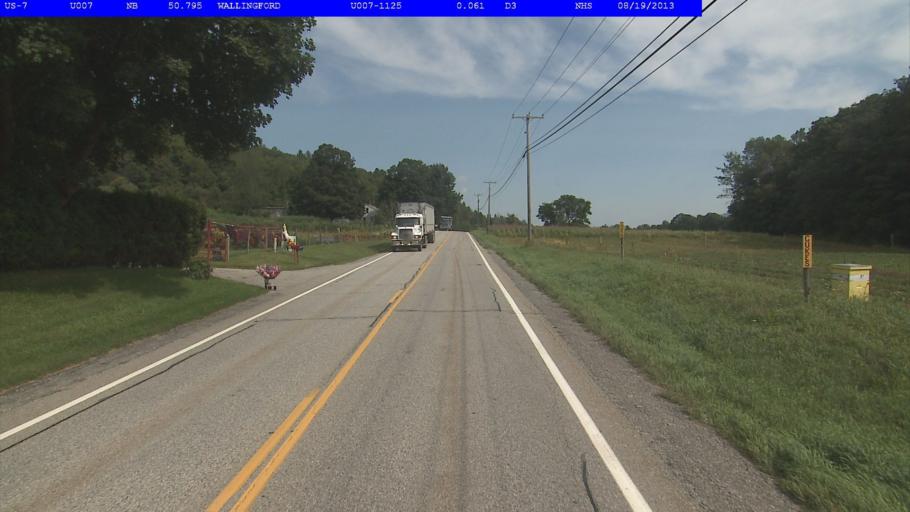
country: US
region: Vermont
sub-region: Rutland County
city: West Rutland
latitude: 43.3983
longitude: -72.9988
